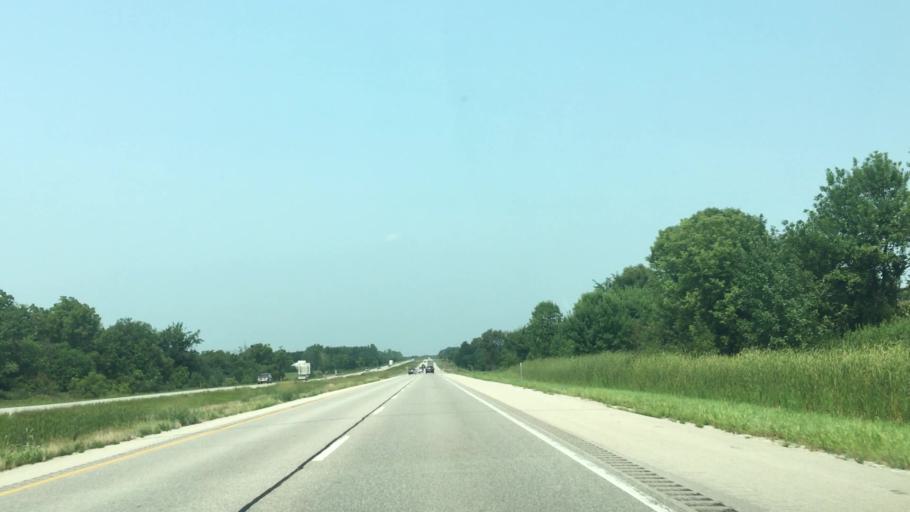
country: US
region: Iowa
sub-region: Linn County
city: Robins
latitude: 42.1084
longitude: -91.7063
